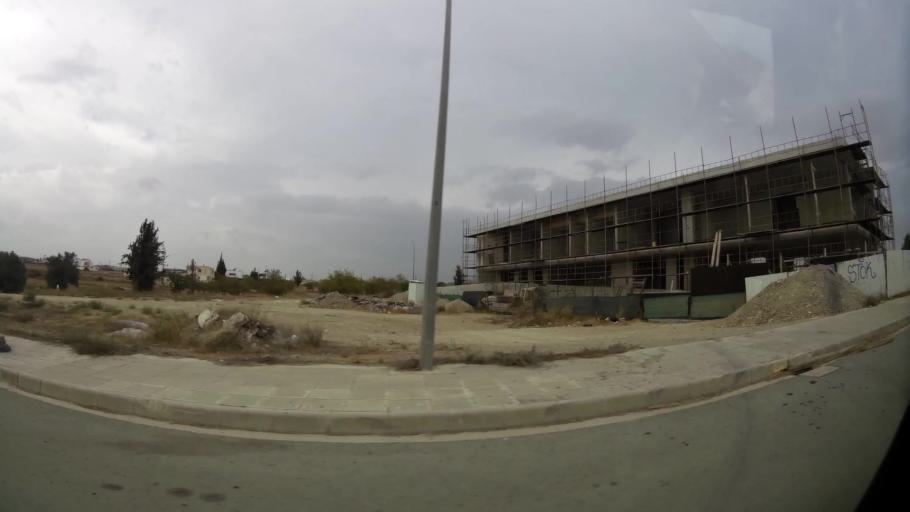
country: CY
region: Lefkosia
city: Geri
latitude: 35.0913
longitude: 33.3923
